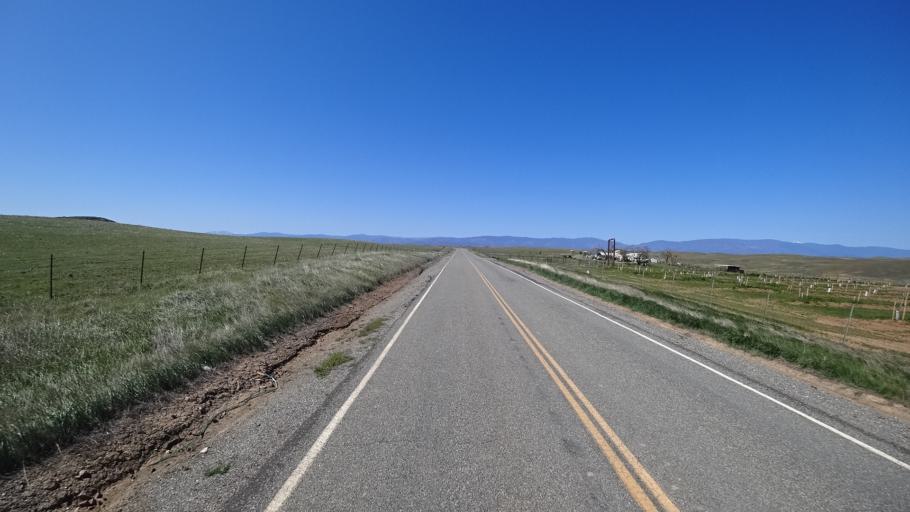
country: US
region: California
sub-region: Glenn County
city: Orland
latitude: 39.8311
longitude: -122.3465
